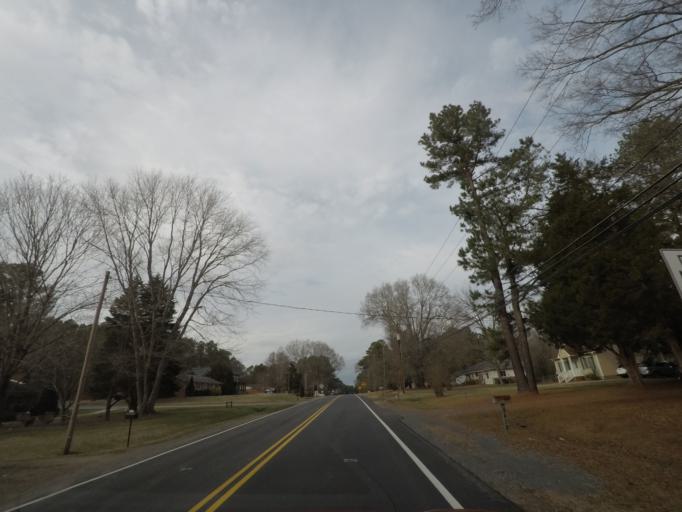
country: US
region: North Carolina
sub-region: Durham County
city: Durham
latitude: 36.0509
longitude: -78.9718
